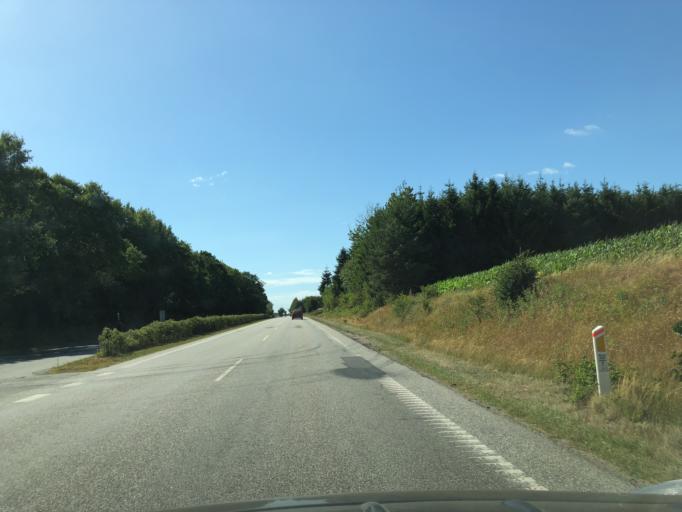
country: DK
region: North Denmark
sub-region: Vesthimmerland Kommune
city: Alestrup
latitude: 56.6183
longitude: 9.6010
